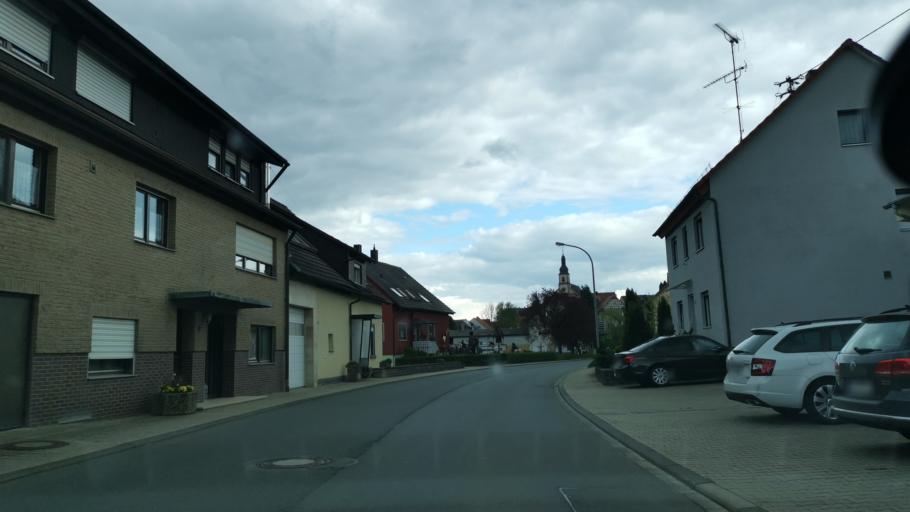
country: DE
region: Baden-Wuerttemberg
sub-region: Karlsruhe Region
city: Buchen
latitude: 49.4992
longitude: 9.3917
